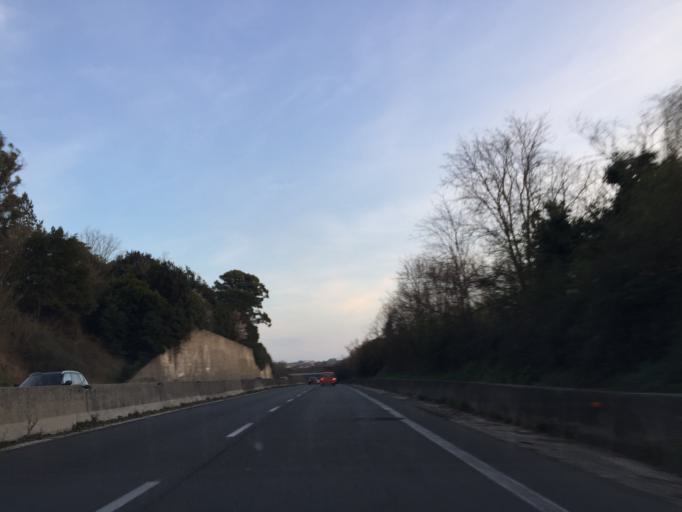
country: IT
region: Latium
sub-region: Citta metropolitana di Roma Capitale
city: Formello
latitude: 42.0222
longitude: 12.4335
